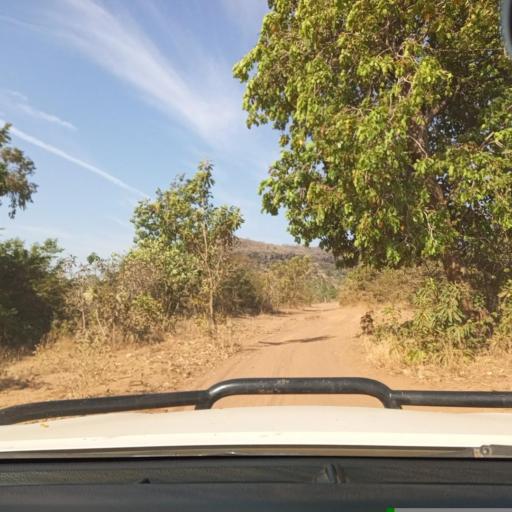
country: ML
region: Bamako
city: Bamako
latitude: 12.5563
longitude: -8.1463
